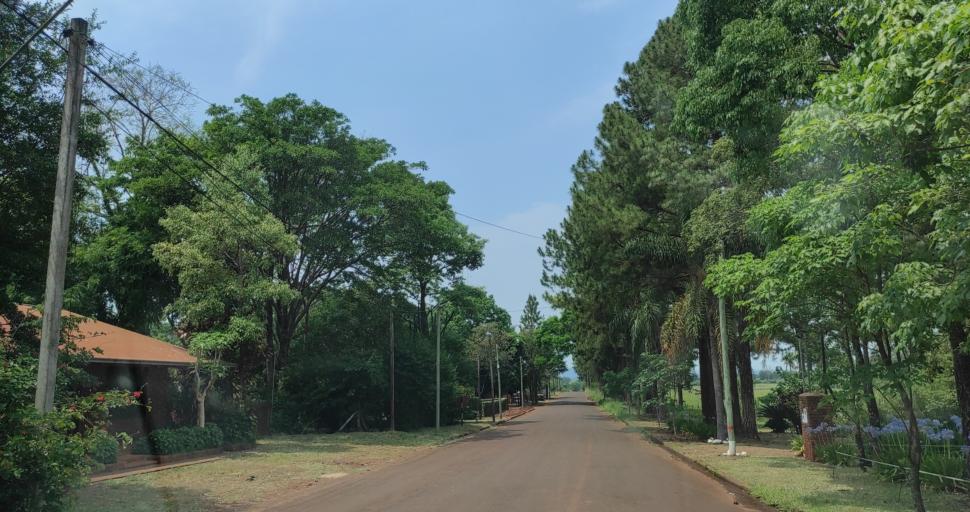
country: AR
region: Misiones
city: Ruiz de Montoya
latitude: -26.9716
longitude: -55.0611
